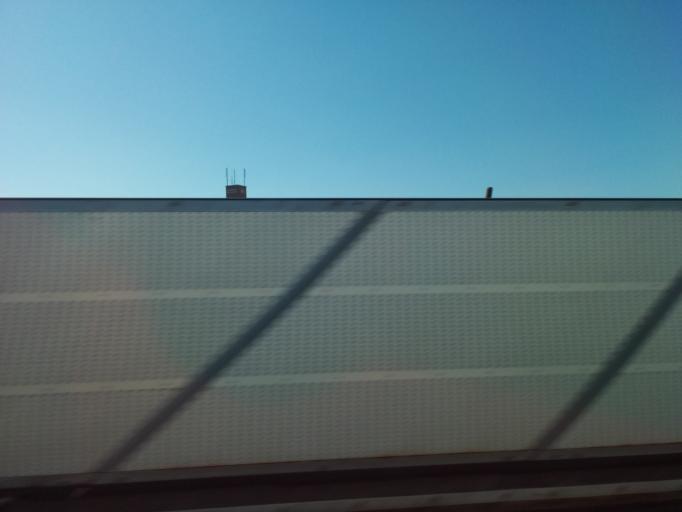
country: JP
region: Aichi
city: Chiryu
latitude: 34.9836
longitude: 137.0467
